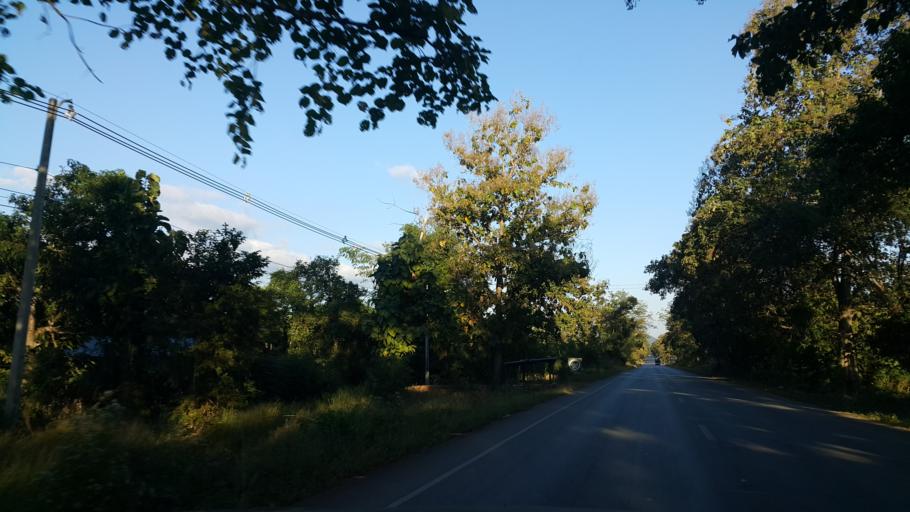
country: TH
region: Sukhothai
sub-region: Amphoe Si Satchanalai
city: Si Satchanalai
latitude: 17.5411
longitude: 99.8192
